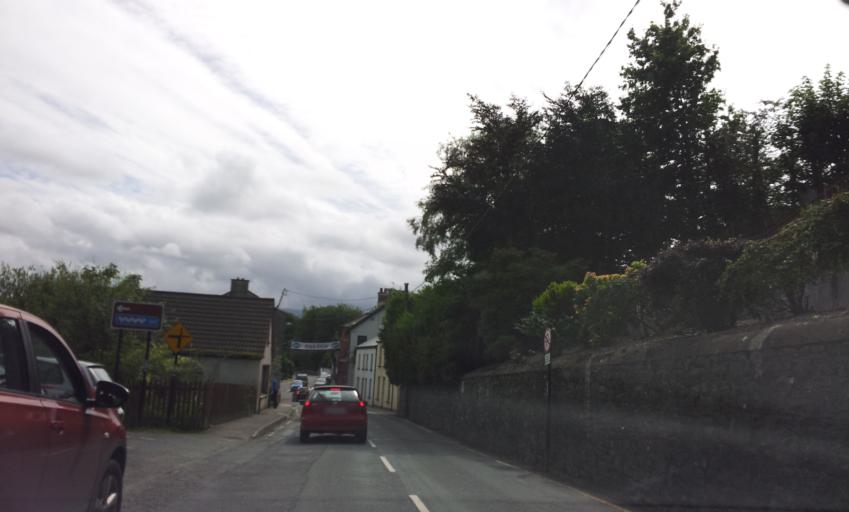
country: IE
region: Munster
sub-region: Ciarrai
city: Killorglin
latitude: 52.1073
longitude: -9.7851
